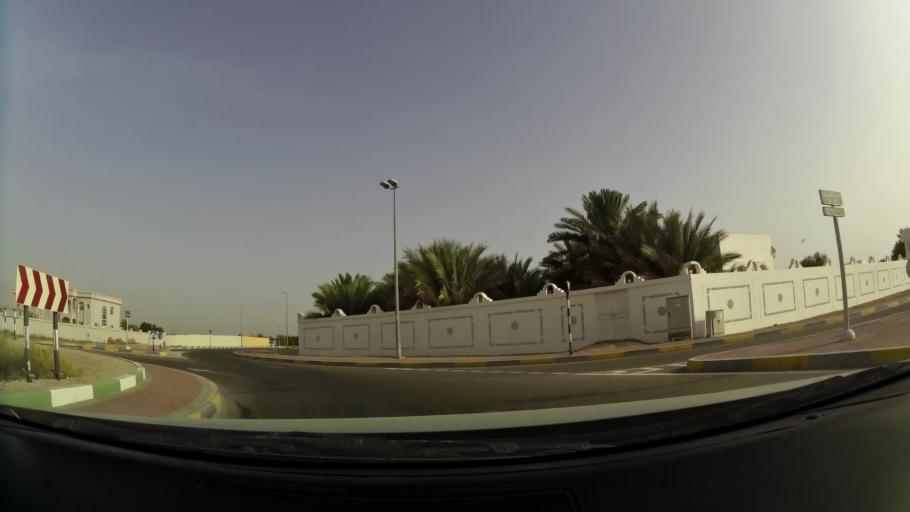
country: AE
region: Abu Dhabi
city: Al Ain
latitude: 24.1322
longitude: 55.6875
